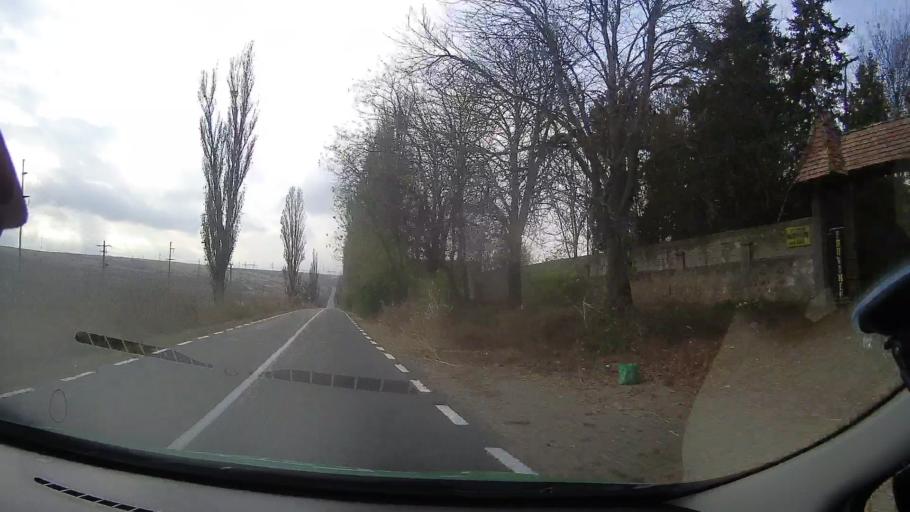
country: RO
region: Constanta
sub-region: Comuna Mircea Voda
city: Satu Nou
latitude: 44.2355
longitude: 28.2302
